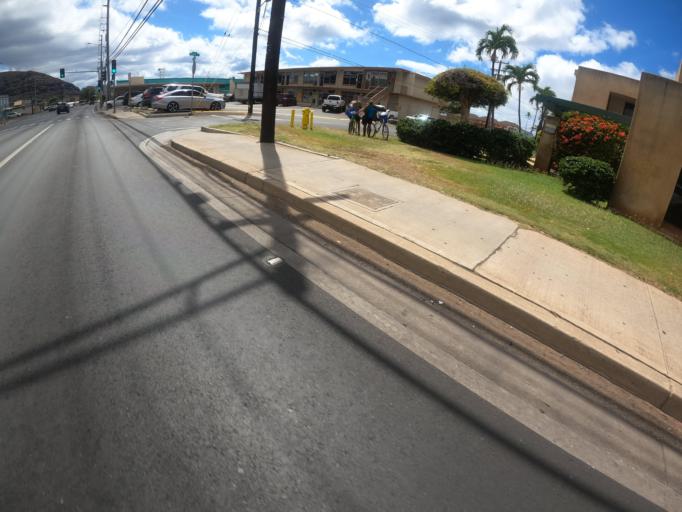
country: US
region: Hawaii
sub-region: Honolulu County
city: Waianae
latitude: 21.4461
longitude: -158.1883
